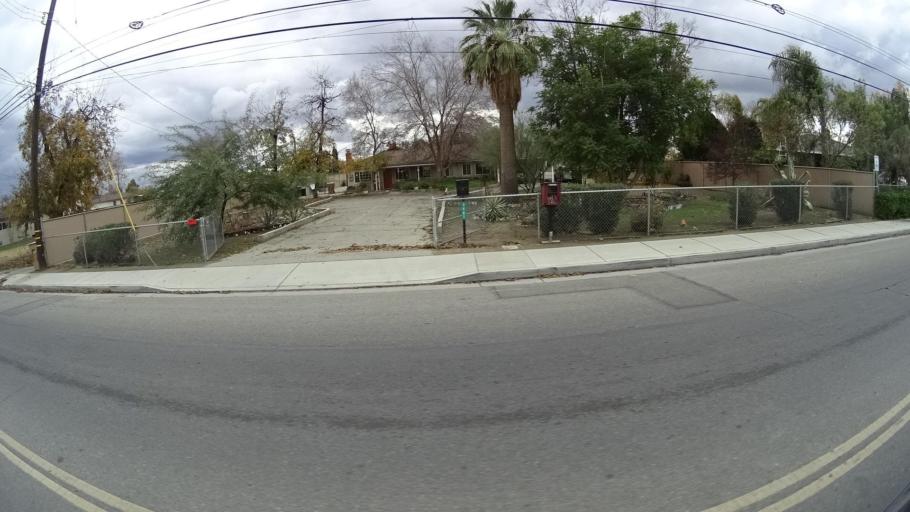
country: US
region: California
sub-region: Kern County
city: Bakersfield
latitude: 35.3467
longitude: -119.0413
